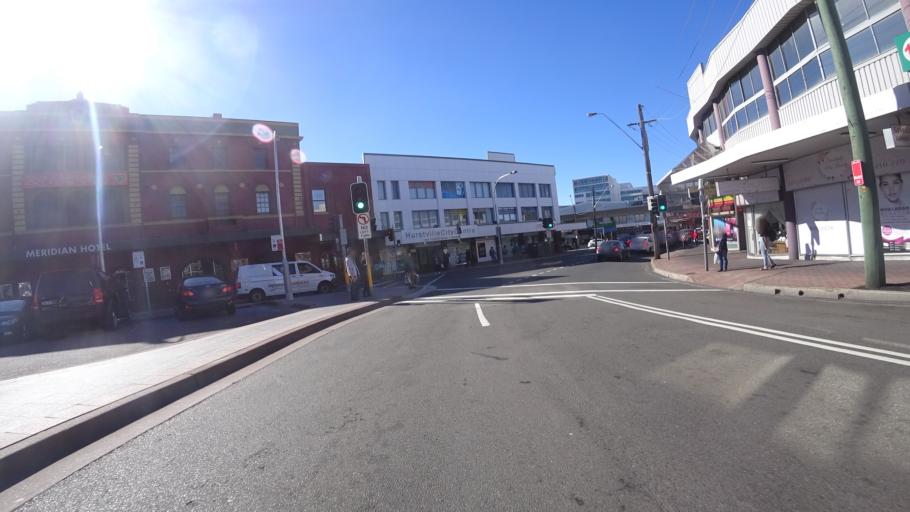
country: AU
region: New South Wales
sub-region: Hurstville
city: Earlwood
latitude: -33.9677
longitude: 151.1049
